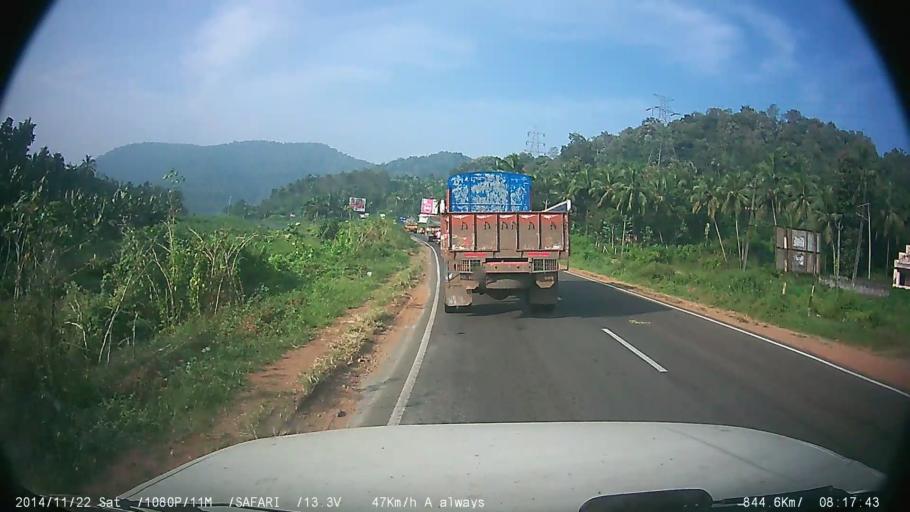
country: IN
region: Kerala
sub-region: Thrissur District
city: Chelakara
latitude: 10.5766
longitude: 76.3943
